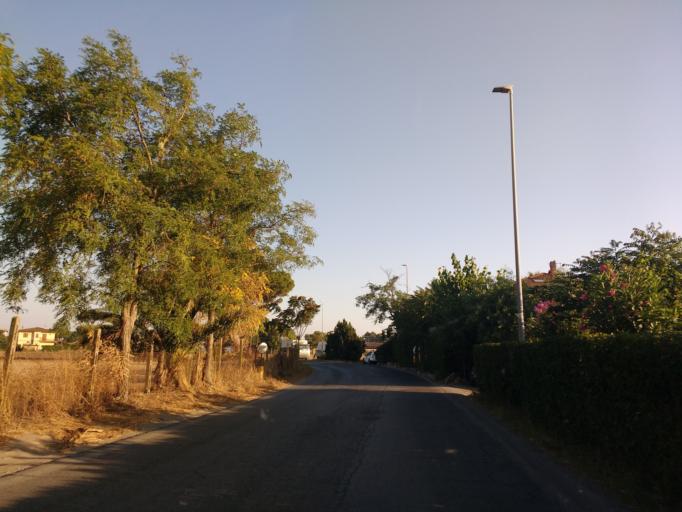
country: IT
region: Latium
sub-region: Citta metropolitana di Roma Capitale
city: Fregene
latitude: 41.8513
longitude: 12.2181
